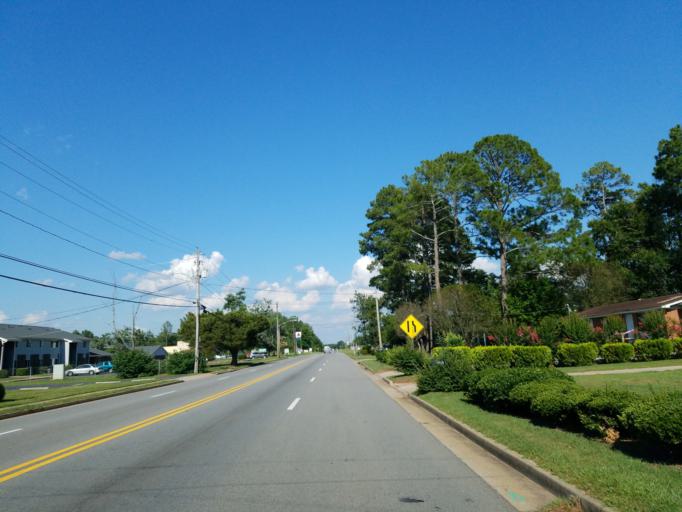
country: US
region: Georgia
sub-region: Peach County
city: Fort Valley
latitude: 32.5539
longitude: -83.8753
